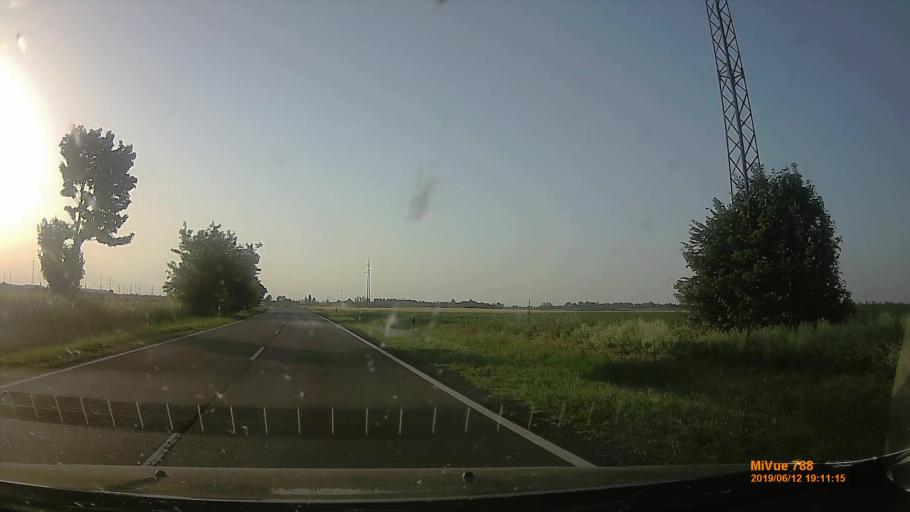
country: HU
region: Bacs-Kiskun
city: Varosfoeld
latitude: 46.8442
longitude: 19.7503
